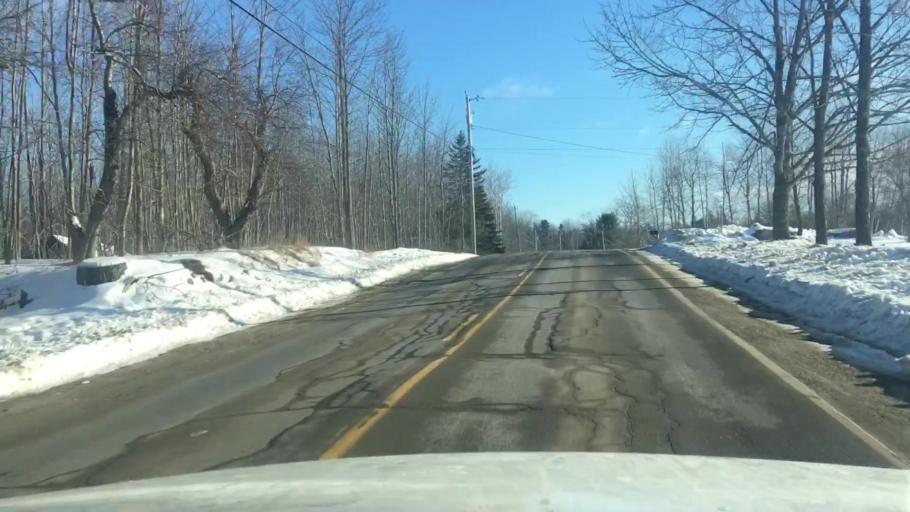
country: US
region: Maine
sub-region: Hancock County
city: Ellsworth
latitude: 44.5946
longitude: -68.4084
